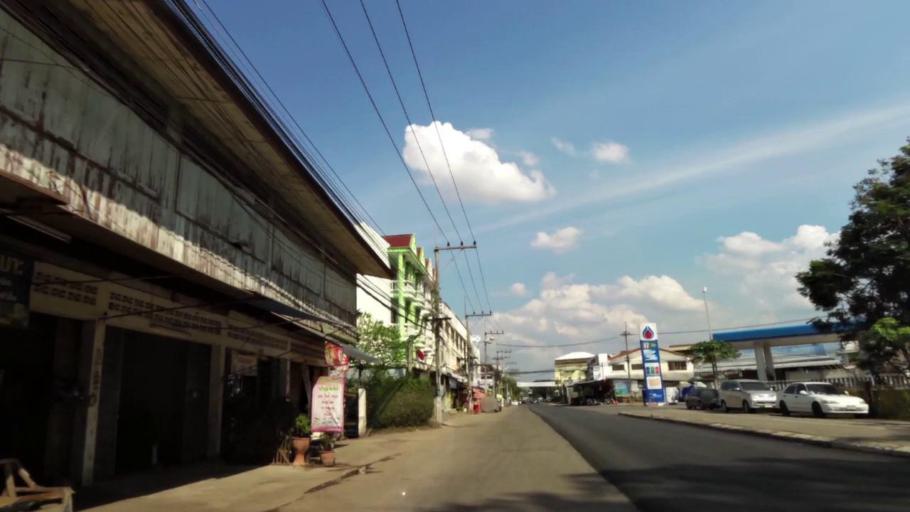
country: TH
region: Phrae
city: Phrae
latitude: 18.1349
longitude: 100.1394
